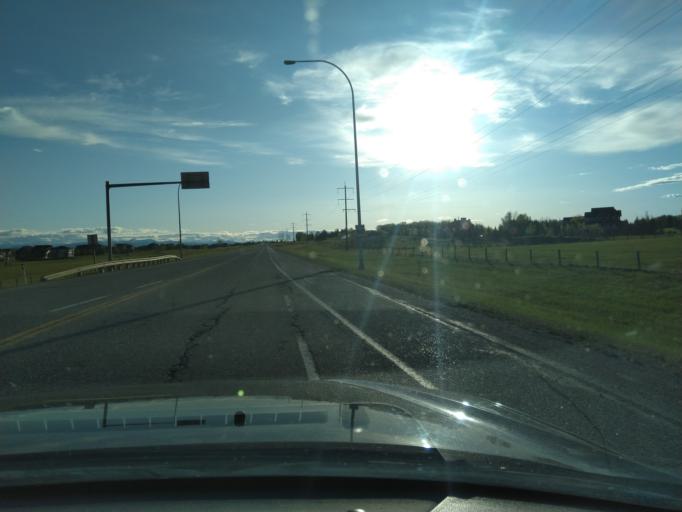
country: CA
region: Alberta
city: Calgary
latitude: 51.0197
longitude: -114.3054
